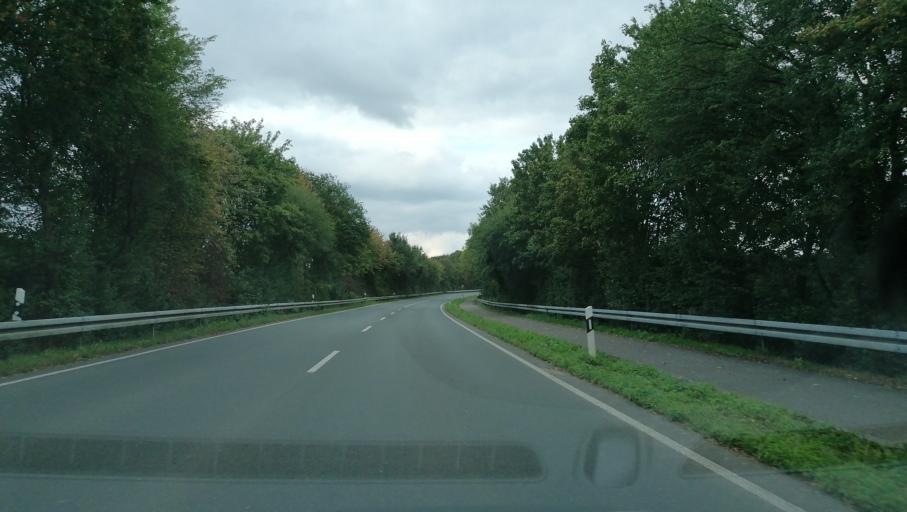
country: DE
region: North Rhine-Westphalia
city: Marl
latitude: 51.6196
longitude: 7.0482
